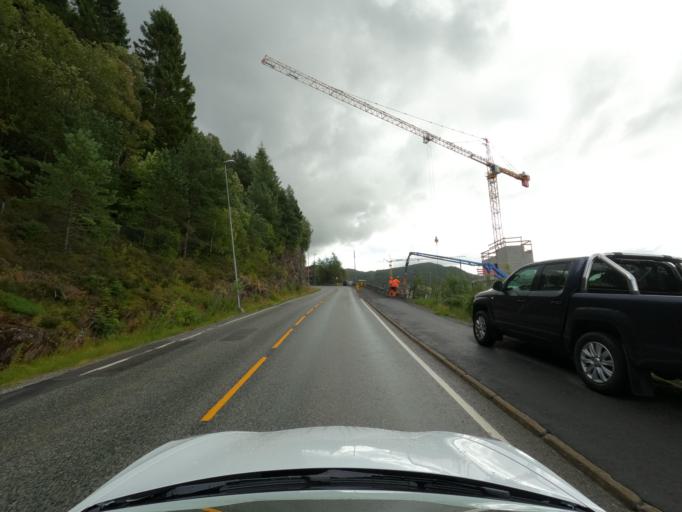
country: NO
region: Hordaland
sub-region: Bergen
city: Hylkje
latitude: 60.4719
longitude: 5.3441
